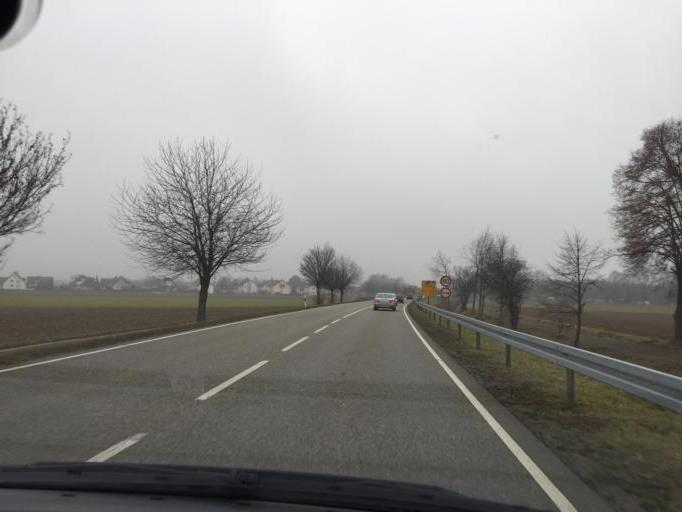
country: DE
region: Baden-Wuerttemberg
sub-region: Freiburg Region
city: Hartheim
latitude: 47.9634
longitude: 7.6612
